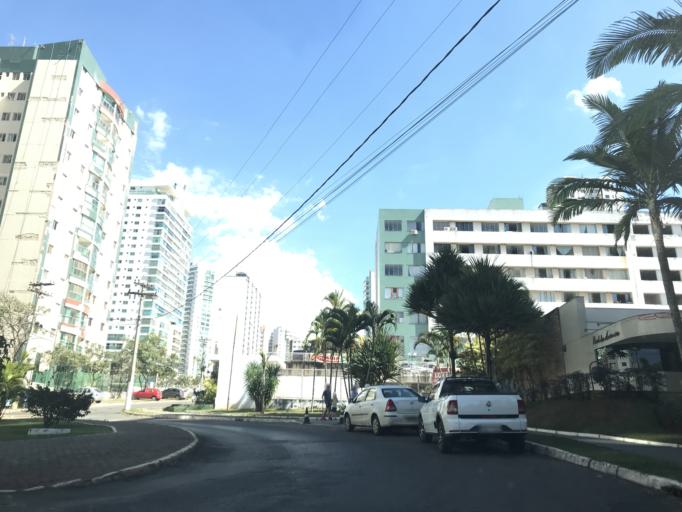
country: BR
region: Federal District
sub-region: Brasilia
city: Brasilia
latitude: -15.8357
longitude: -48.0291
